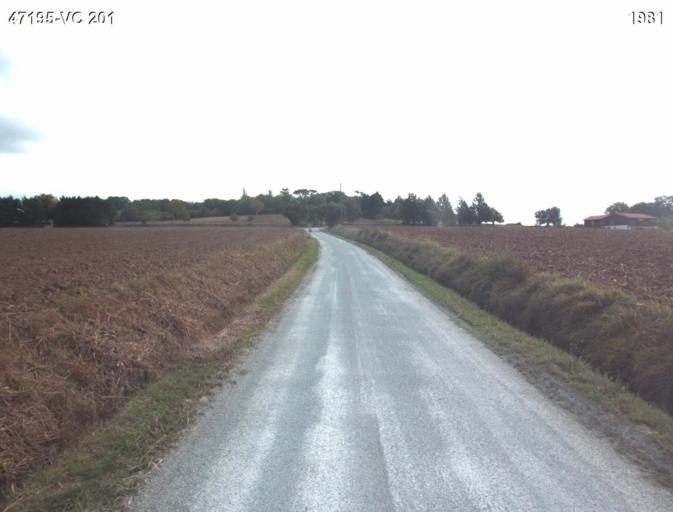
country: FR
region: Aquitaine
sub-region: Departement du Lot-et-Garonne
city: Barbaste
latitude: 44.1334
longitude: 0.2975
